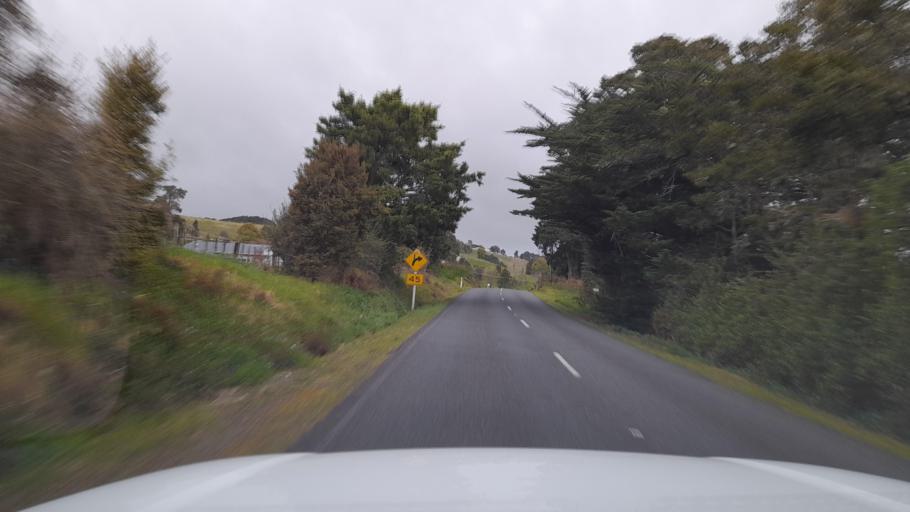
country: NZ
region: Northland
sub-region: Whangarei
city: Maungatapere
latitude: -35.6527
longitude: 174.2201
